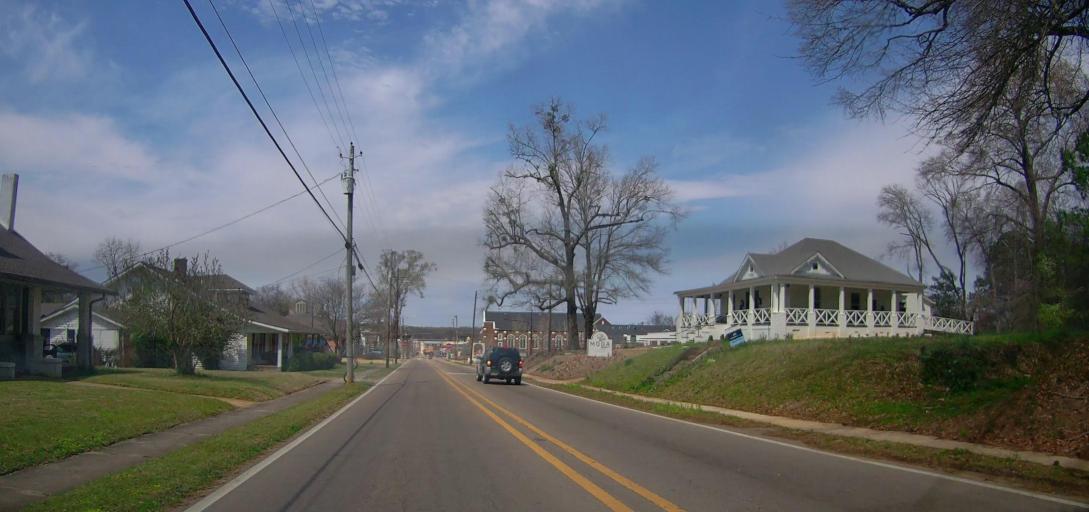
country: US
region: Mississippi
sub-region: Union County
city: New Albany
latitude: 34.4908
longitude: -89.0045
